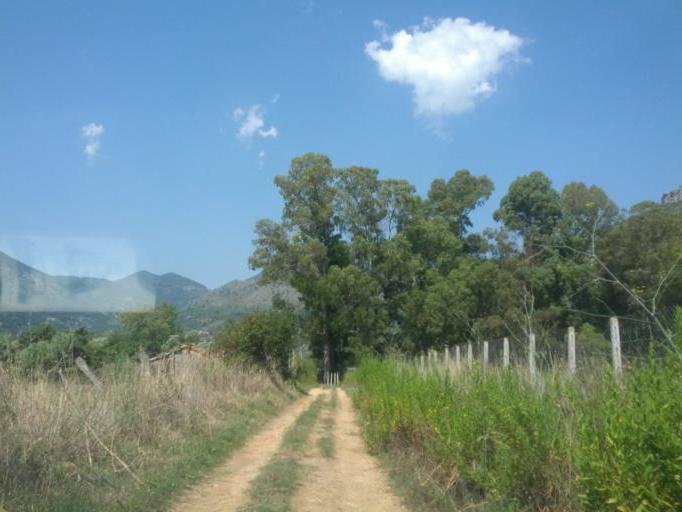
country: IT
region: Latium
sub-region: Provincia di Latina
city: Monte San Biagio
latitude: 41.3655
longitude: 13.3561
